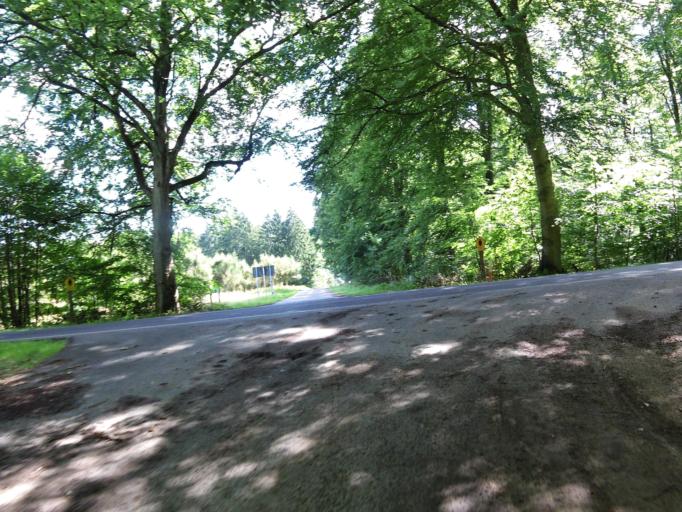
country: DE
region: Brandenburg
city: Templin
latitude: 53.2432
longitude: 13.4503
